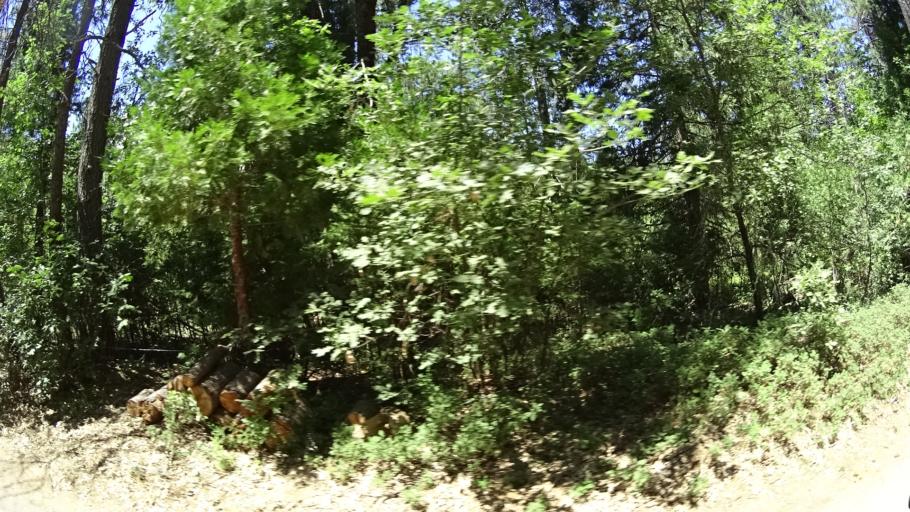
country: US
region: California
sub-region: Calaveras County
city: Arnold
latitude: 38.2575
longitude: -120.4187
